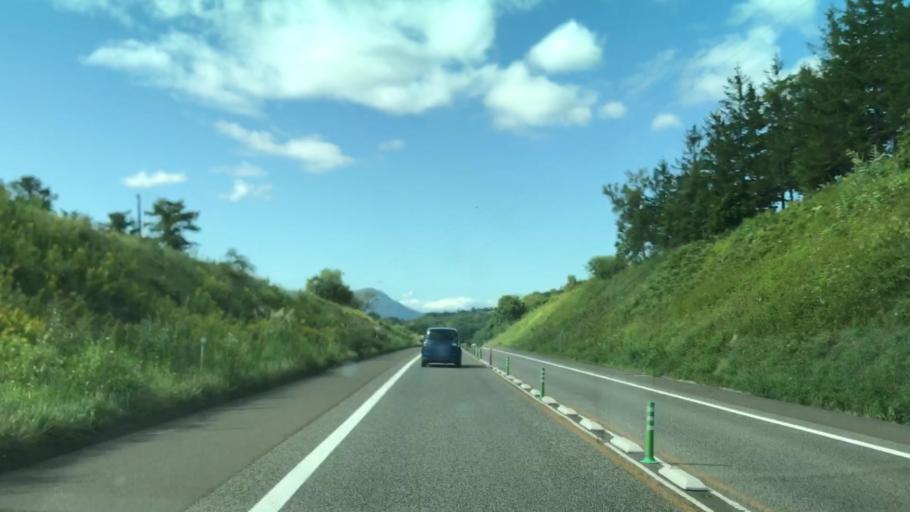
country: JP
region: Hokkaido
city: Date
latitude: 42.4253
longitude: 140.9281
